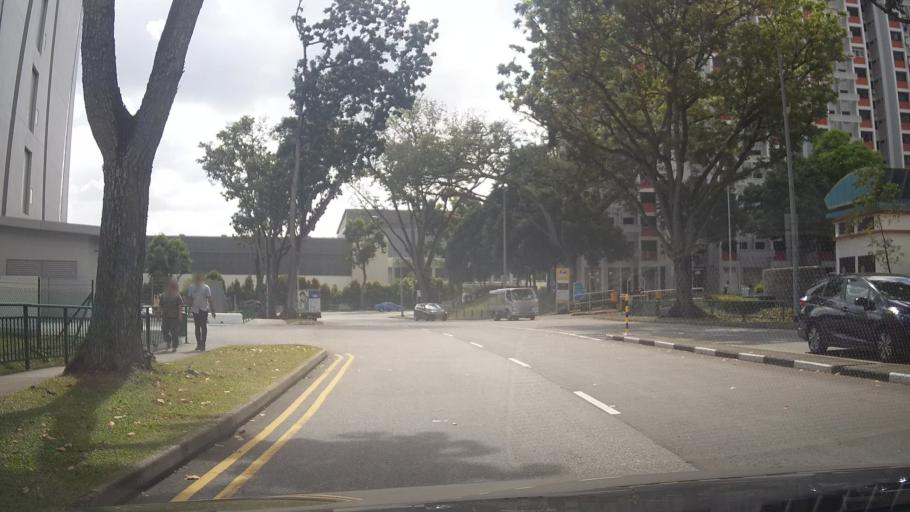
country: MY
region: Johor
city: Johor Bahru
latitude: 1.4422
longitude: 103.7789
